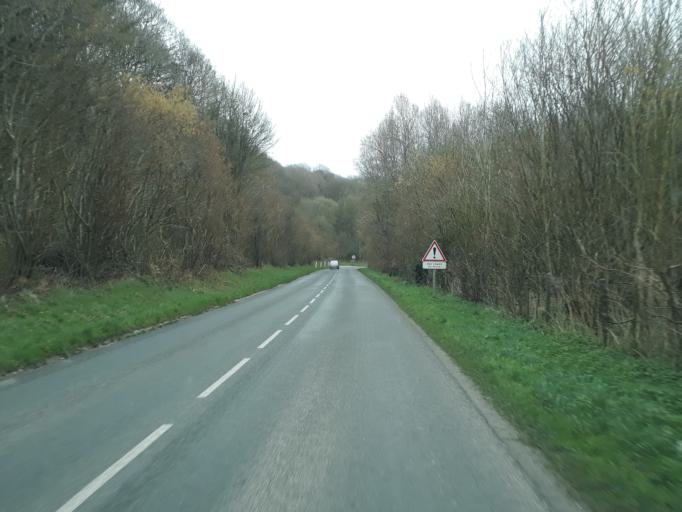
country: FR
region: Haute-Normandie
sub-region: Departement de la Seine-Maritime
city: Les Loges
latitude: 49.6783
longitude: 0.2560
